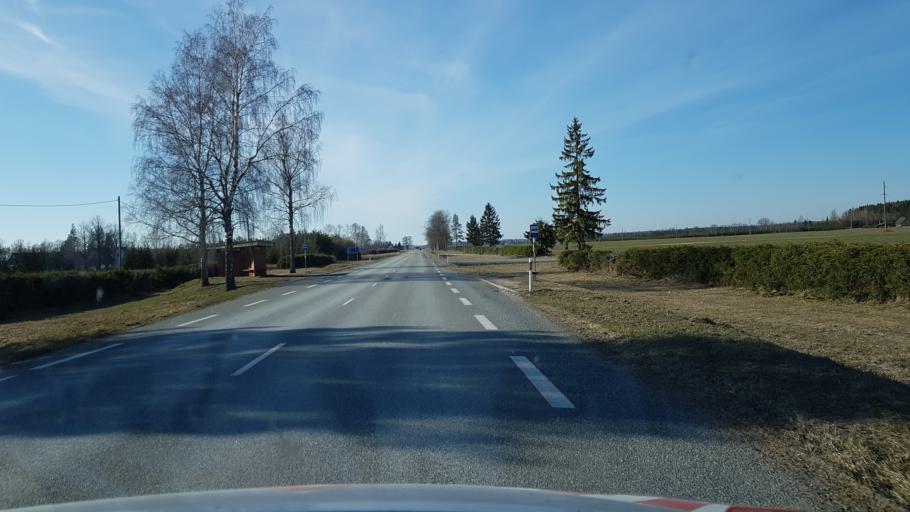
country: EE
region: Laeaene-Virumaa
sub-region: Vinni vald
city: Vinni
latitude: 59.2218
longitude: 26.5318
